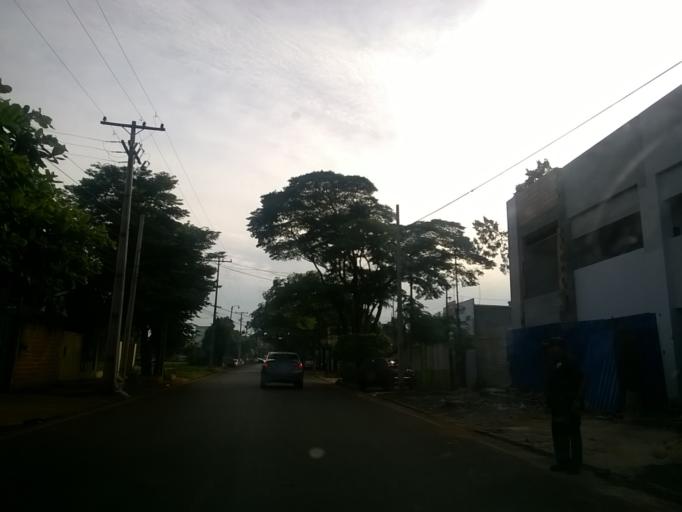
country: PY
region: Alto Parana
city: Ciudad del Este
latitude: -25.5008
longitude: -54.6336
